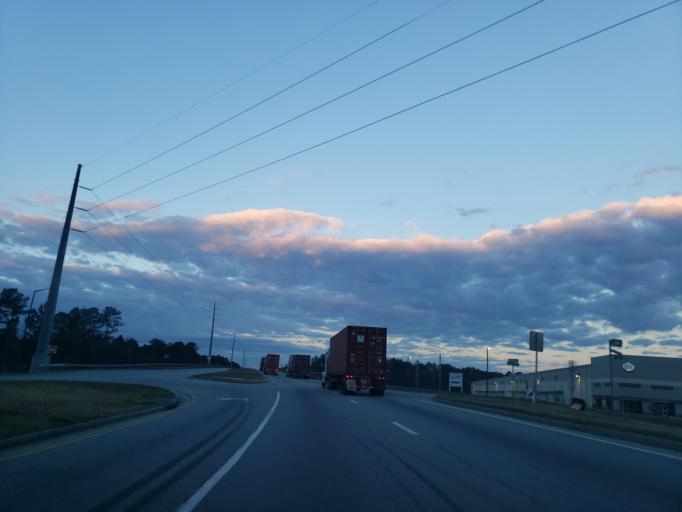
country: US
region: Georgia
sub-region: Chatham County
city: Port Wentworth
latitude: 32.1648
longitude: -81.1970
